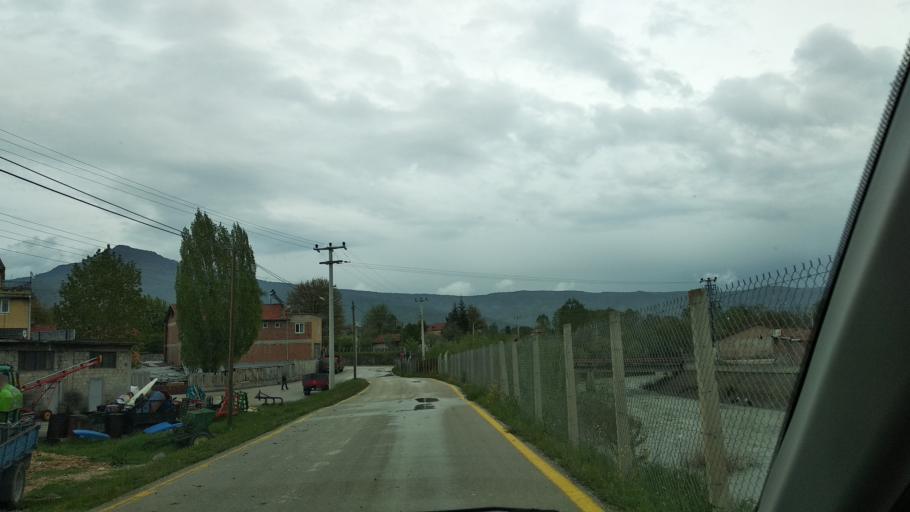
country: TR
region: Bolu
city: Seben
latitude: 40.4072
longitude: 31.5717
